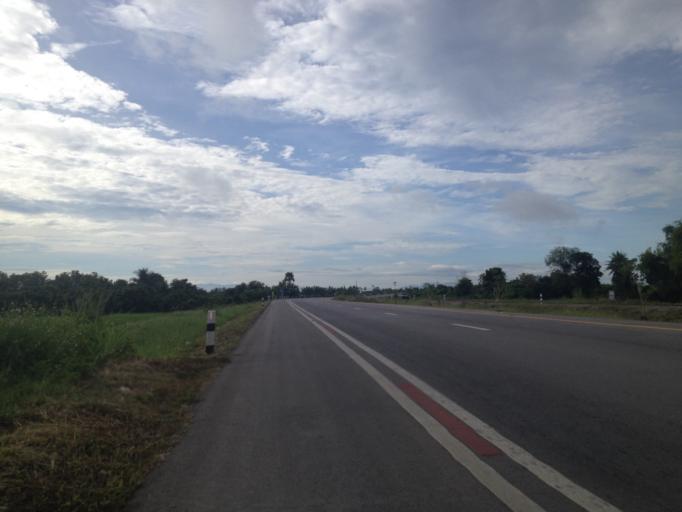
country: TH
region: Chiang Mai
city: San Pa Tong
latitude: 18.5683
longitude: 98.8490
